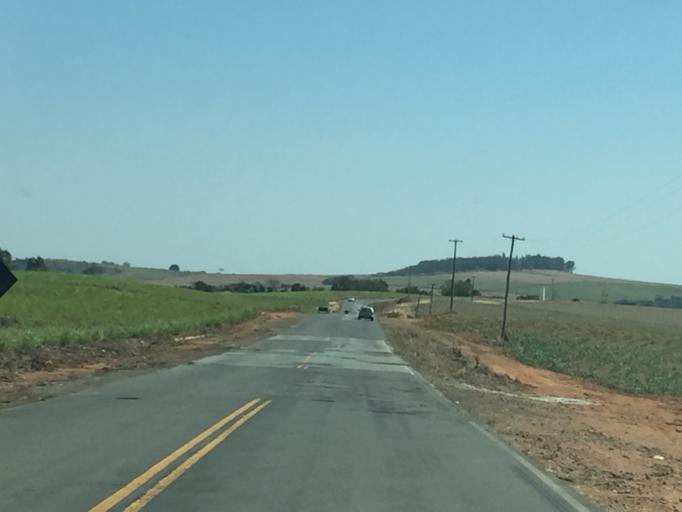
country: BR
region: Sao Paulo
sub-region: Itapira
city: Itapira
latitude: -22.3921
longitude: -46.8606
